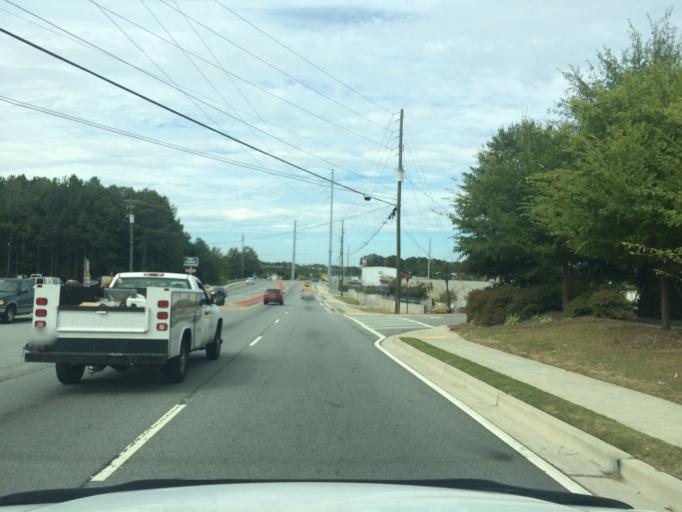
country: US
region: Georgia
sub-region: Cobb County
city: Kennesaw
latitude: 34.0484
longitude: -84.6065
